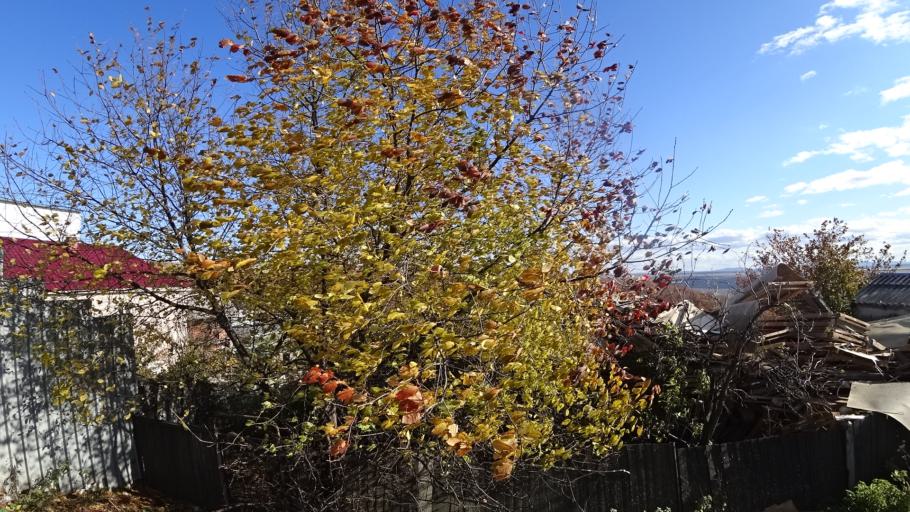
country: RU
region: Khabarovsk Krai
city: Amursk
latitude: 50.2329
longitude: 136.9204
